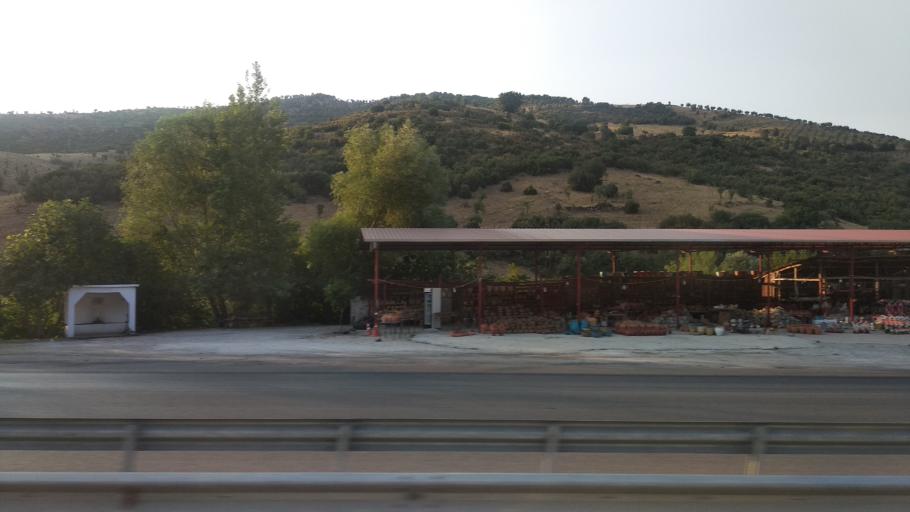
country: TR
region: Manisa
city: Menye
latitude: 38.5491
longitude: 28.4574
